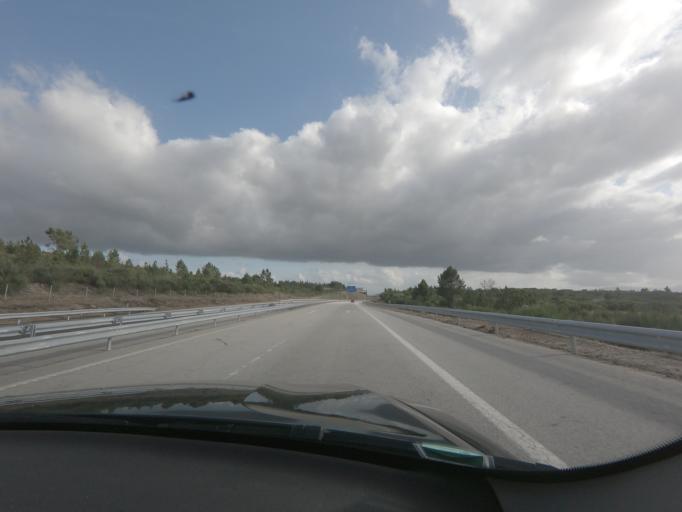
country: PT
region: Viseu
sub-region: Castro Daire
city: Castro Daire
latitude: 40.9427
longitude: -7.9044
